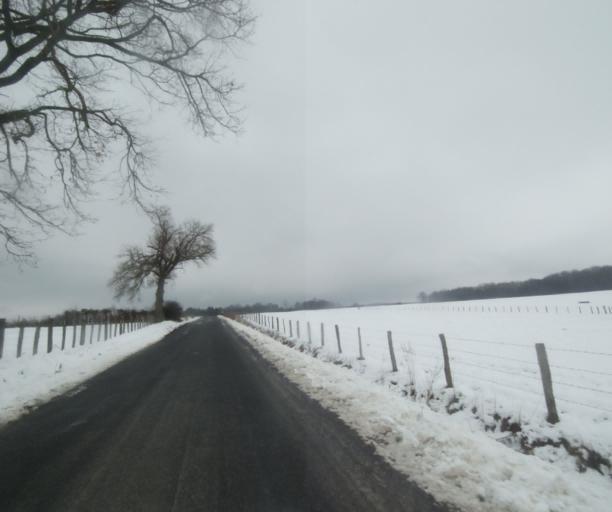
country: FR
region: Champagne-Ardenne
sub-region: Departement de la Haute-Marne
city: Montier-en-Der
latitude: 48.4695
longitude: 4.8094
